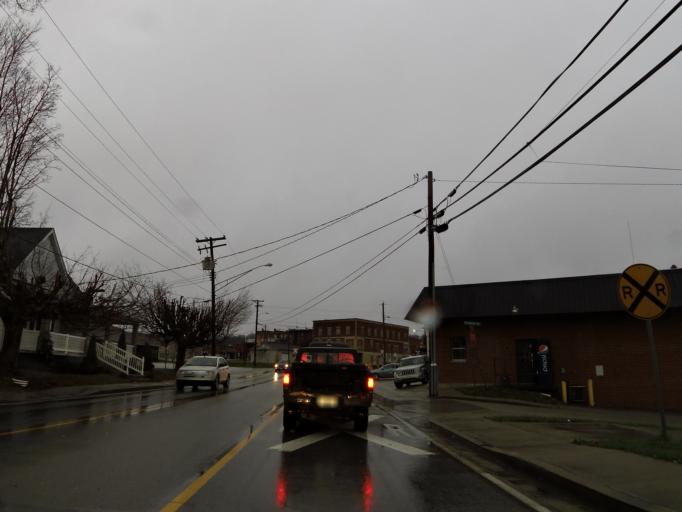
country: US
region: Kentucky
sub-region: Rockcastle County
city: Mount Vernon
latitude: 37.3549
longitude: -84.3403
